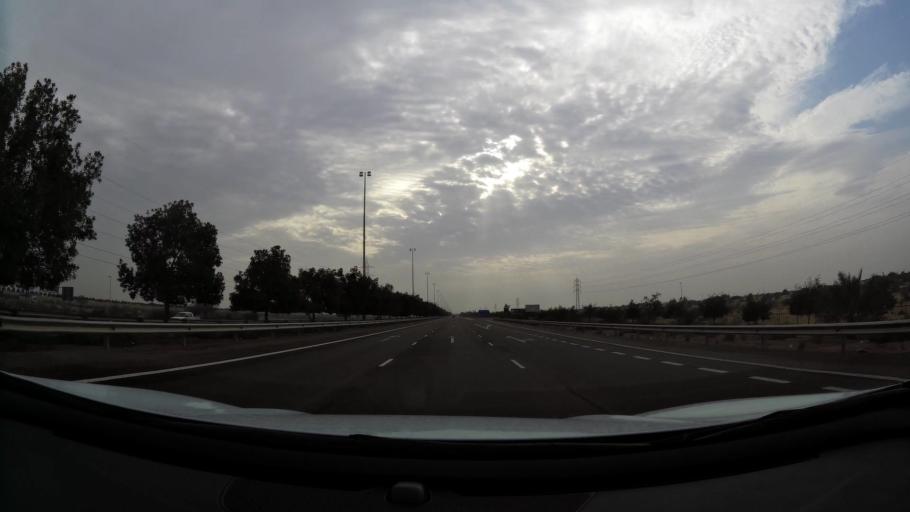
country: AE
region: Abu Dhabi
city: Abu Dhabi
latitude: 24.2024
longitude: 54.9062
